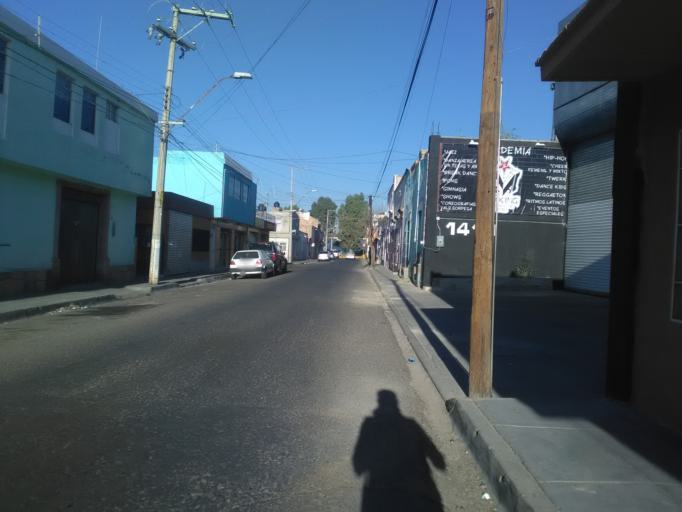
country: MX
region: Durango
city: Victoria de Durango
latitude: 24.0338
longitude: -104.6786
